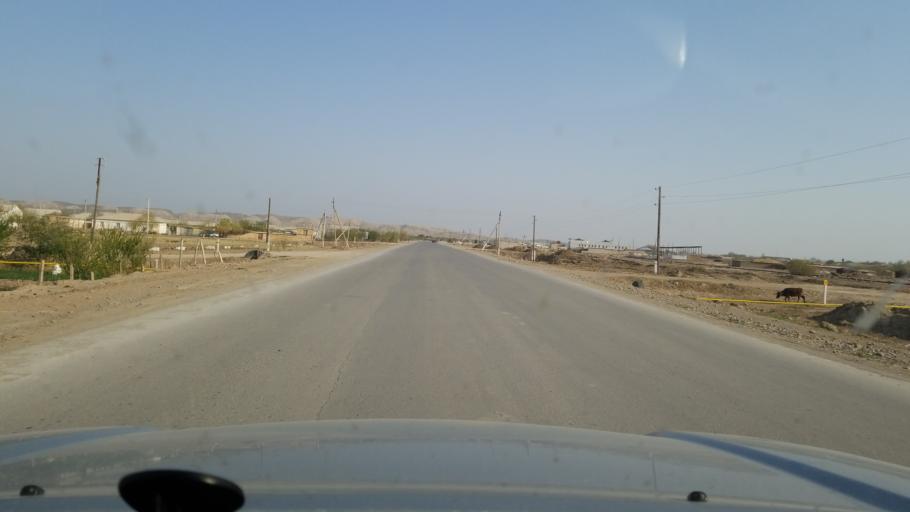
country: AF
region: Jowzjan
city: Khamyab
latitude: 37.5388
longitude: 65.8674
